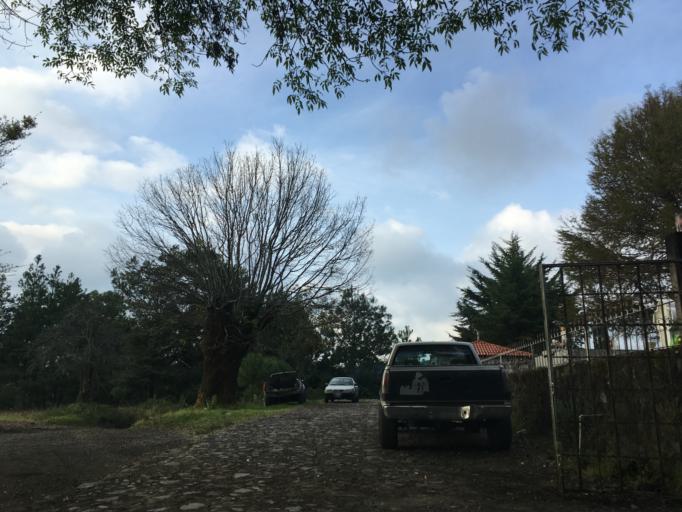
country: MX
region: Michoacan
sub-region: Uruapan
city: Santa Ana Zirosto
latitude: 19.5710
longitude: -102.2888
